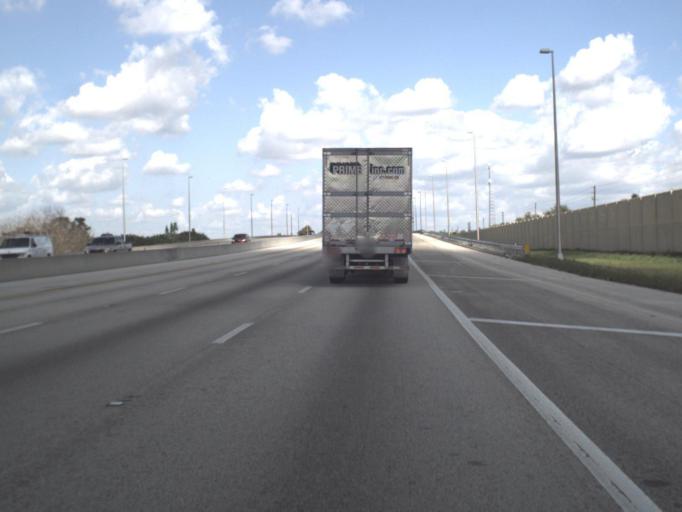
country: US
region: Florida
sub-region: Palm Beach County
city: Villages of Oriole
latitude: 26.4485
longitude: -80.1743
